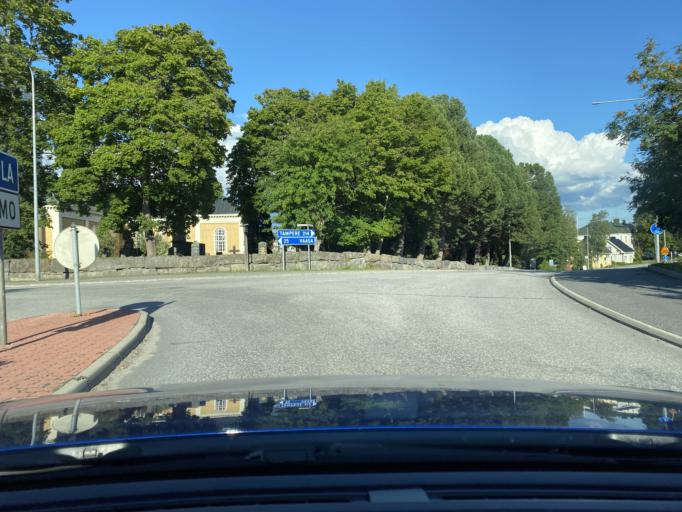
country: FI
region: Ostrobothnia
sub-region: Kyroenmaa
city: Laihia
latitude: 62.9760
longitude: 22.0113
